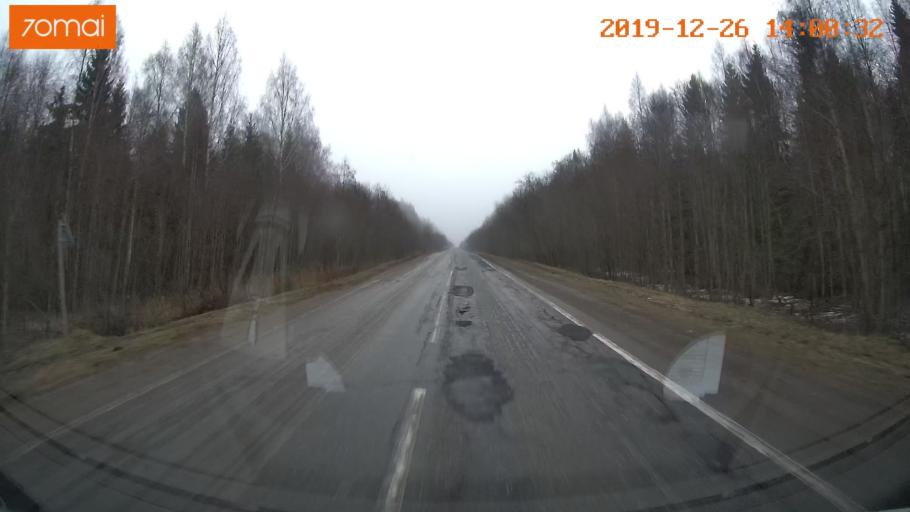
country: RU
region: Jaroslavl
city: Poshekhon'ye
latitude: 58.5575
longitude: 38.7451
